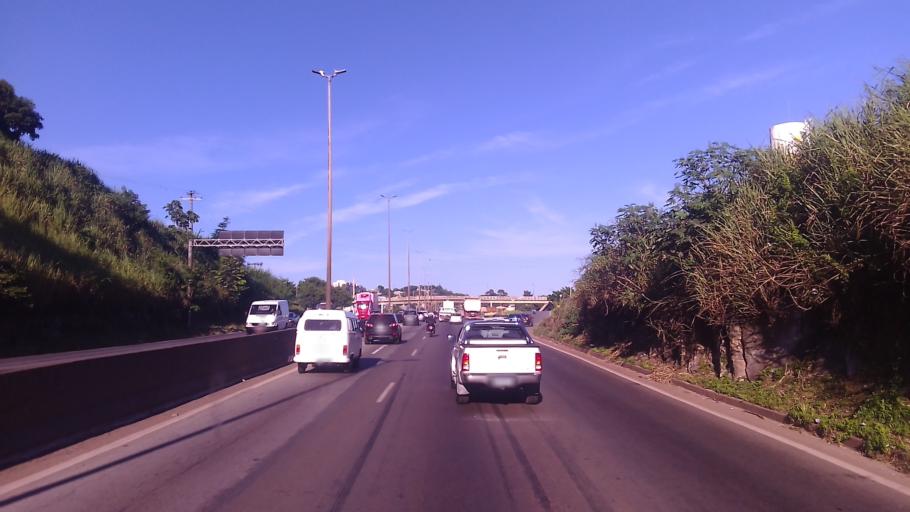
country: BR
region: Minas Gerais
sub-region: Belo Horizonte
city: Belo Horizonte
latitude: -19.8674
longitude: -43.9352
